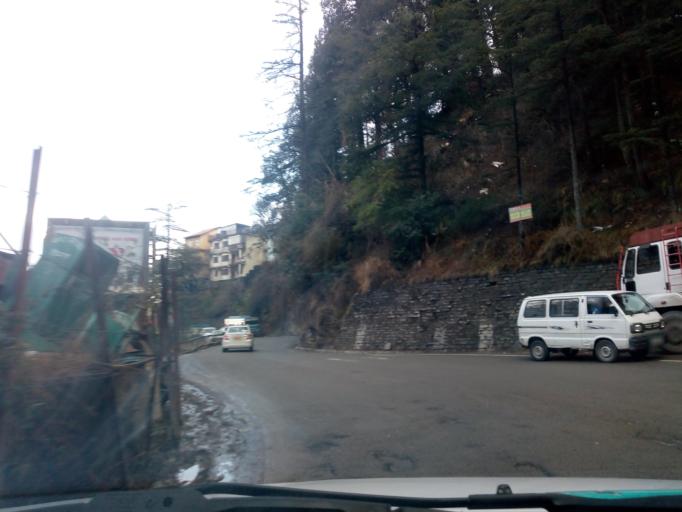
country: IN
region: Himachal Pradesh
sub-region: Shimla
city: Shimla
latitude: 31.1049
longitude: 77.1862
